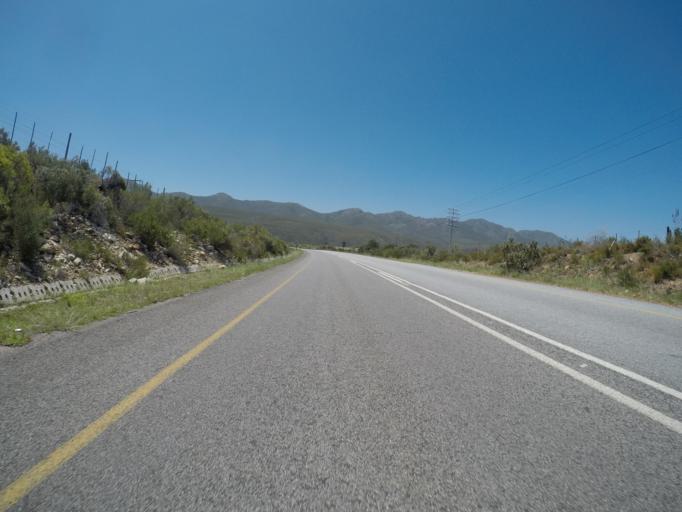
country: ZA
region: Eastern Cape
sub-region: Cacadu District Municipality
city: Kareedouw
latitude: -33.9485
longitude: 24.3034
